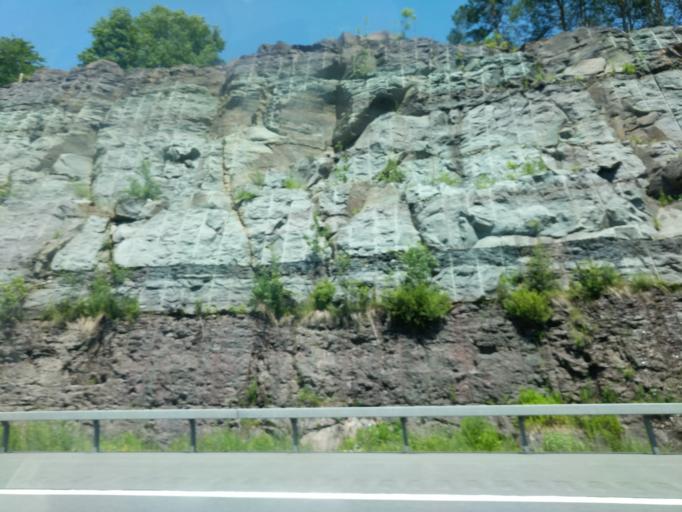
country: US
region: New York
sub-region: Sullivan County
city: Rock Hill
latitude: 41.6353
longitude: -74.6151
